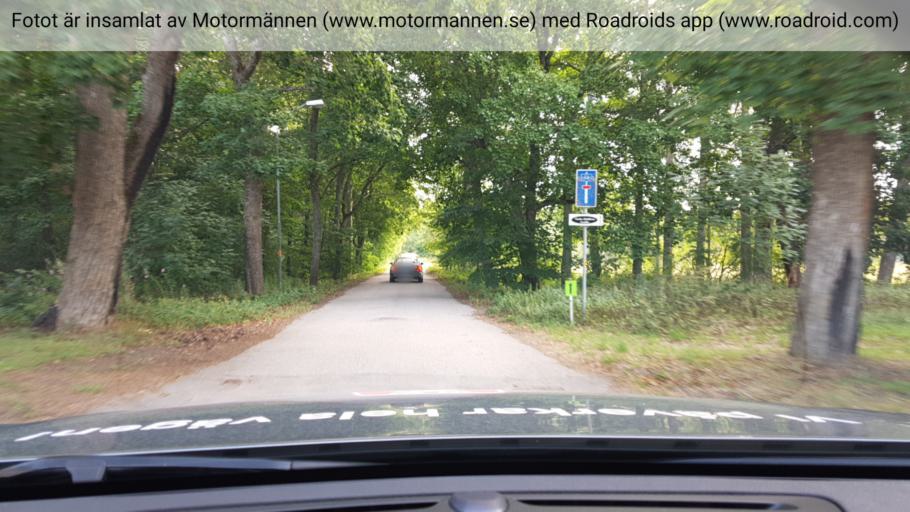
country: SE
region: Uppsala
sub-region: Heby Kommun
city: Tarnsjo
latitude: 60.2886
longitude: 16.8922
